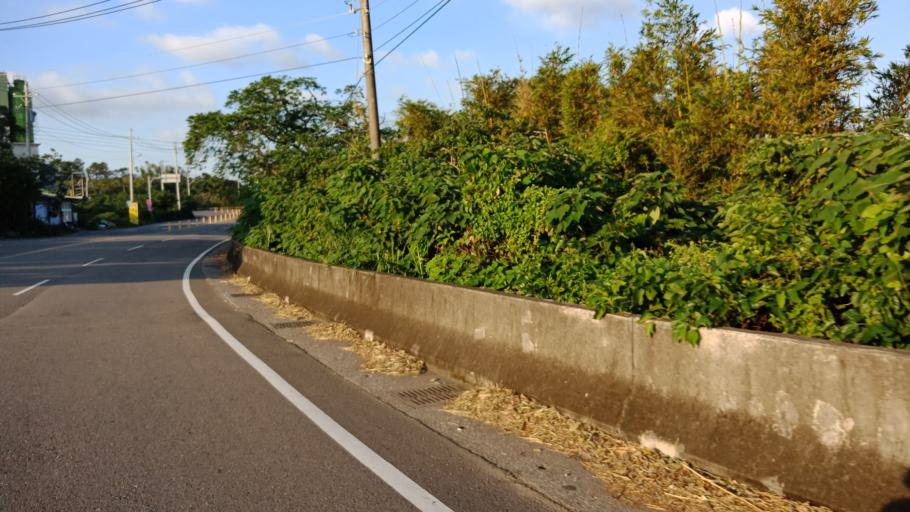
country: TW
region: Taiwan
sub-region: Hsinchu
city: Hsinchu
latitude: 24.7574
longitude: 120.9989
